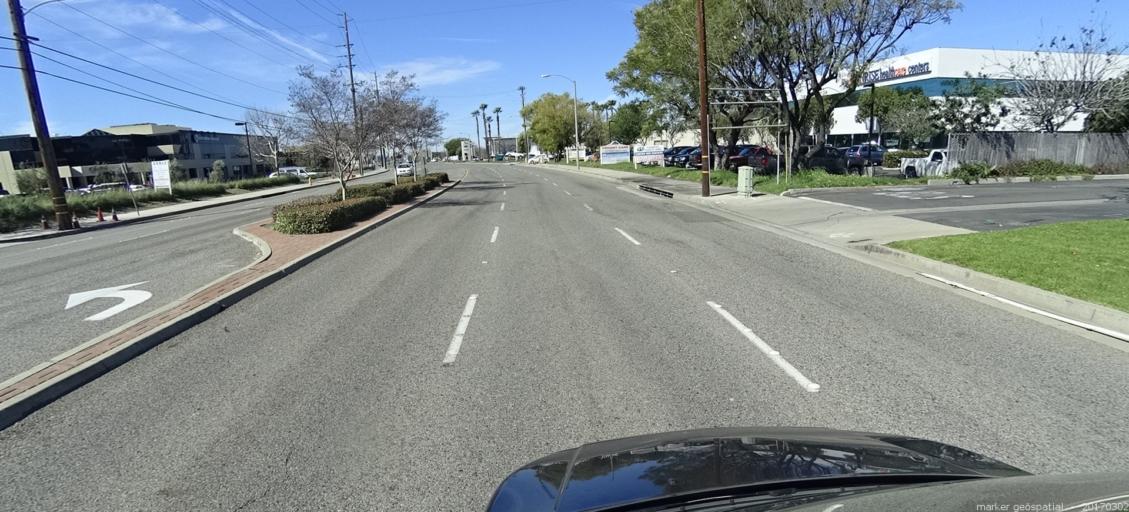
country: US
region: California
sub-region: Orange County
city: Yorba Linda
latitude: 33.8600
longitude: -117.7953
